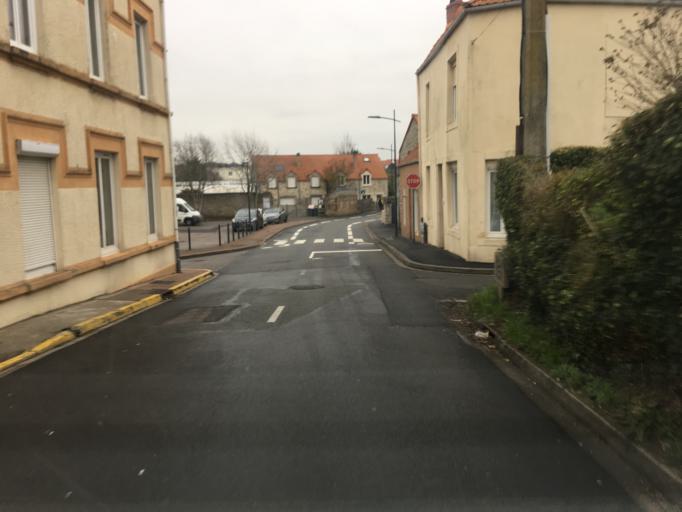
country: FR
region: Nord-Pas-de-Calais
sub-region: Departement du Pas-de-Calais
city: Wimereux
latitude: 50.7656
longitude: 1.6156
